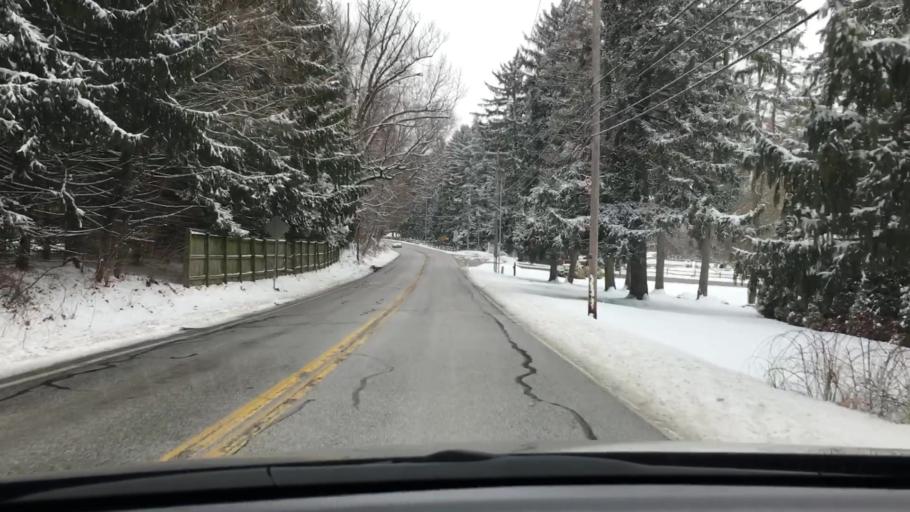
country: US
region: Pennsylvania
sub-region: York County
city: Grantley
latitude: 39.9363
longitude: -76.7257
